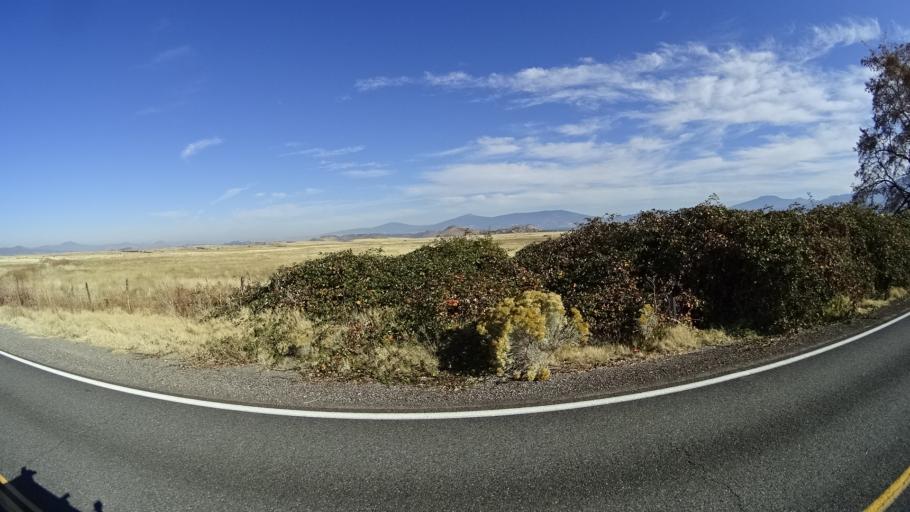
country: US
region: California
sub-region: Siskiyou County
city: Weed
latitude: 41.4694
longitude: -122.4736
